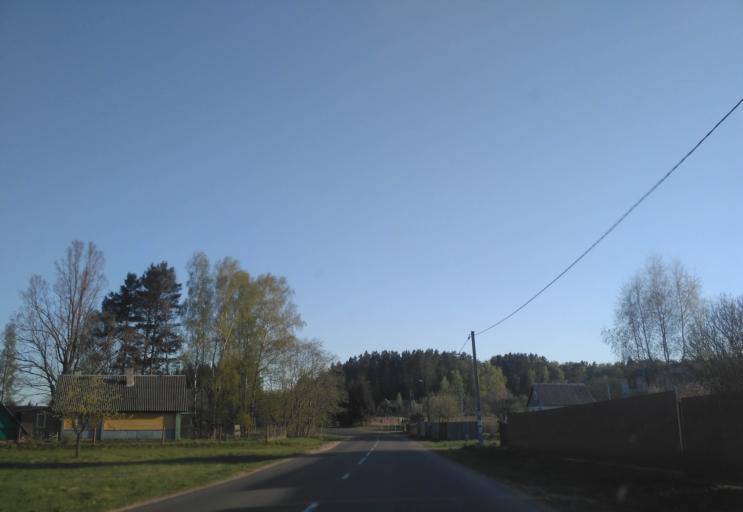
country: BY
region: Minsk
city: Radashkovichy
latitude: 54.1303
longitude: 27.2010
